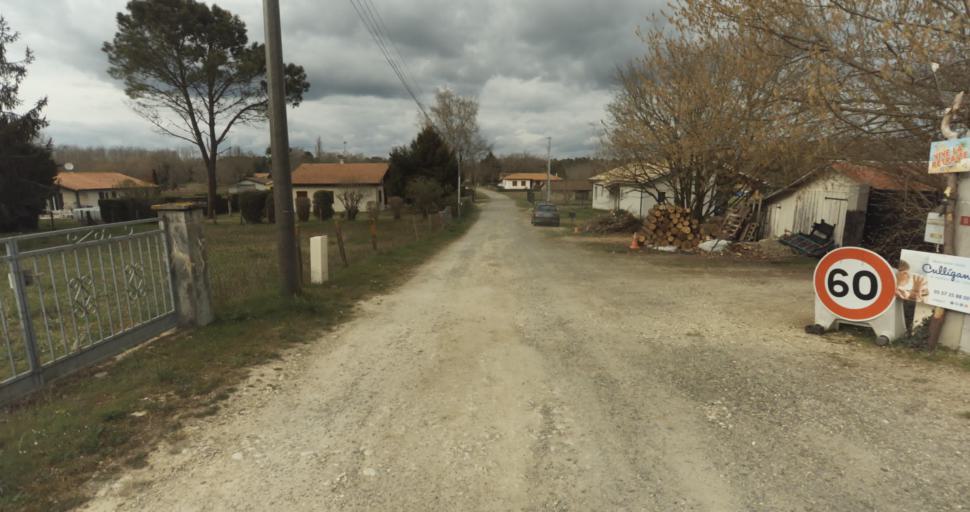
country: FR
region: Aquitaine
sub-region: Departement des Landes
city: Roquefort
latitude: 44.0403
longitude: -0.3286
